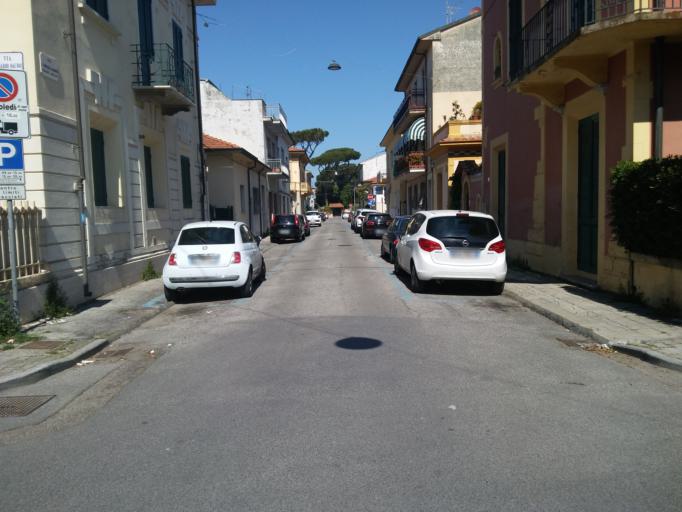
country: IT
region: Tuscany
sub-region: Provincia di Lucca
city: Viareggio
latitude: 43.8792
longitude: 10.2450
